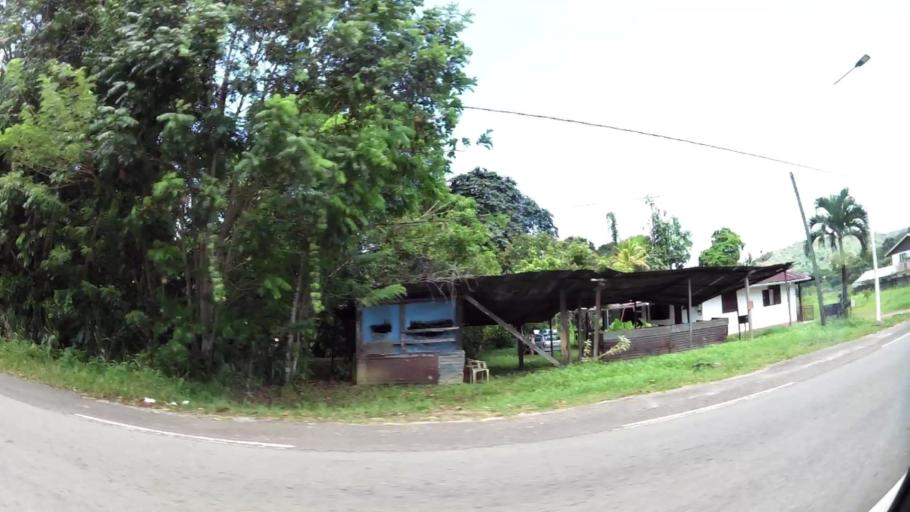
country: GF
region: Guyane
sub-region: Guyane
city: Matoury
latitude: 4.8555
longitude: -52.3336
